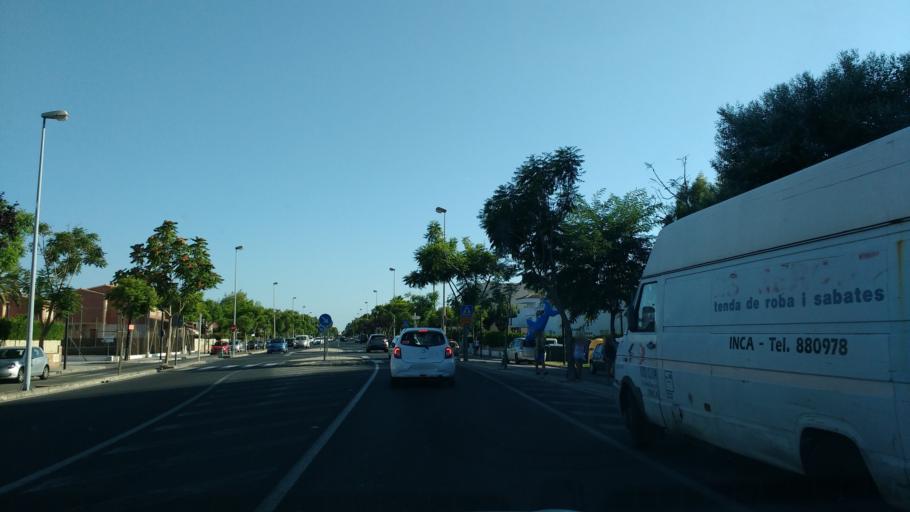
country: ES
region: Balearic Islands
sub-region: Illes Balears
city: Port d'Alcudia
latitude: 39.8286
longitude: 3.1160
